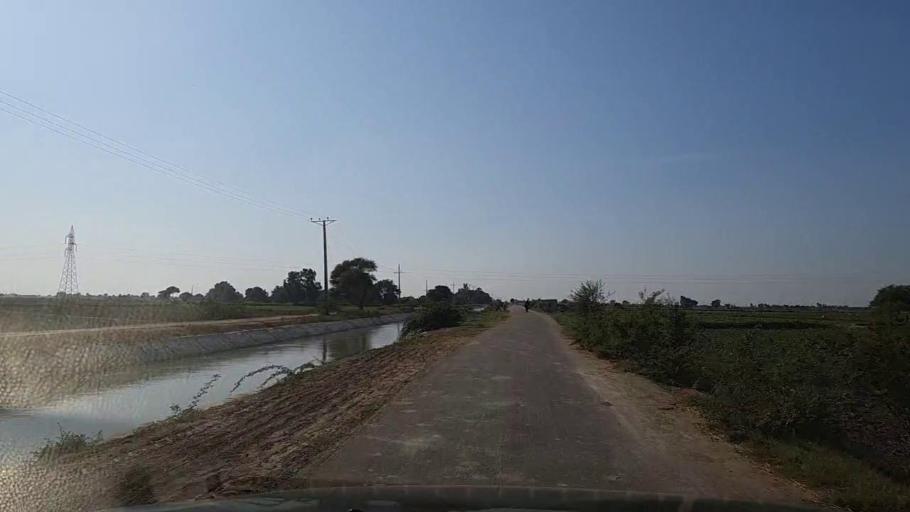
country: PK
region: Sindh
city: Thatta
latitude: 24.5963
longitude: 67.8172
